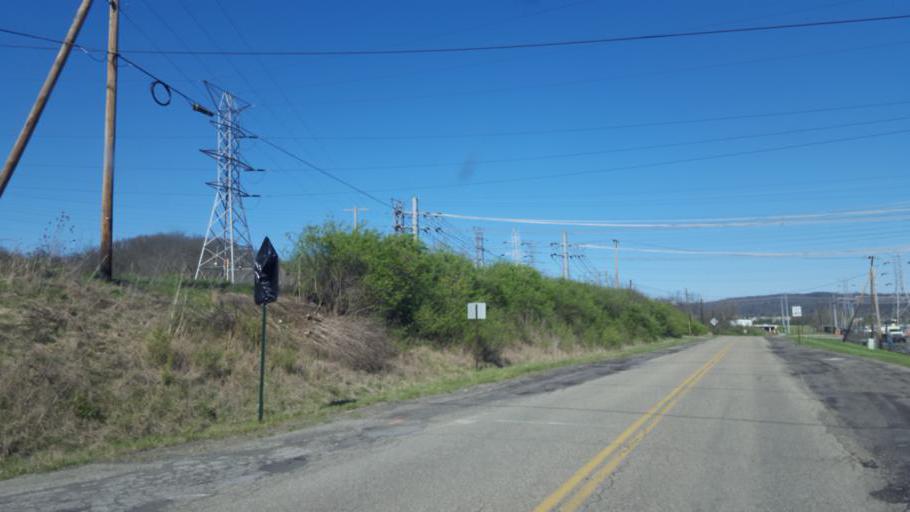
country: US
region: Ohio
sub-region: Jefferson County
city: Brilliant
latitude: 40.2552
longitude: -80.6485
